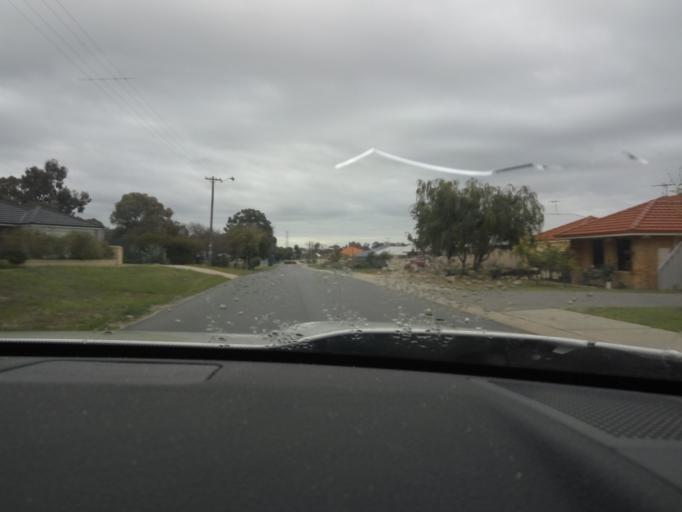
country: AU
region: Western Australia
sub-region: City of Cockburn
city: South Lake
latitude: -32.1134
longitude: 115.8461
